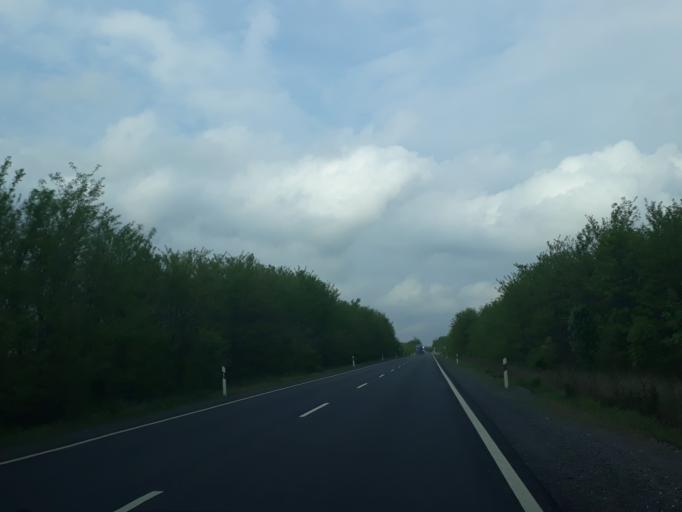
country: HU
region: Szabolcs-Szatmar-Bereg
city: Nyirtass
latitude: 48.1320
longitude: 22.0151
